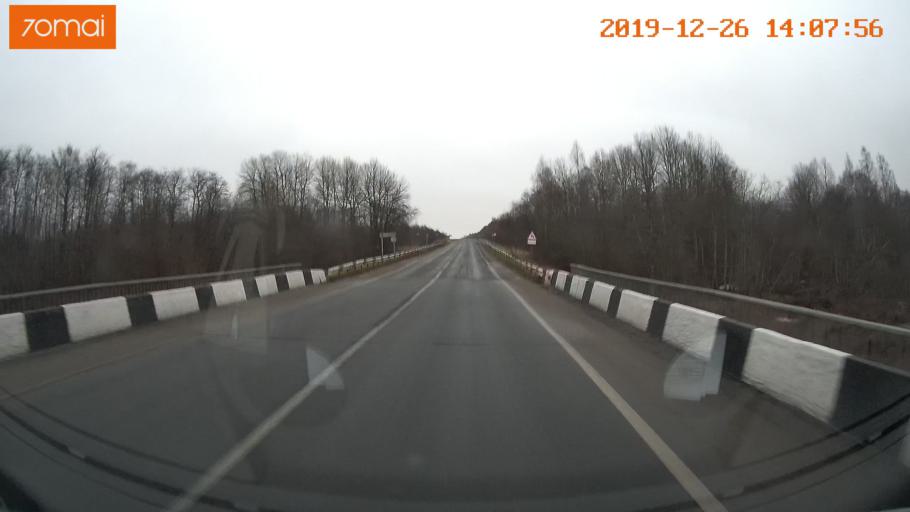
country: RU
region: Jaroslavl
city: Poshekhon'ye
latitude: 58.5089
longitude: 38.9007
